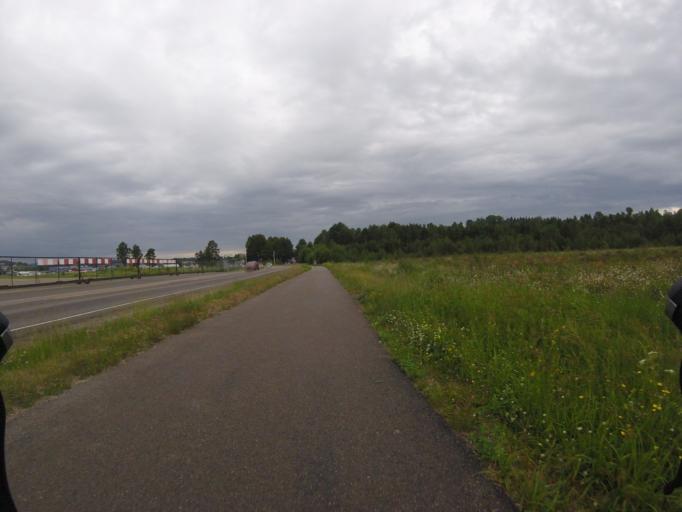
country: NO
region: Akershus
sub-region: Skedsmo
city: Lillestrom
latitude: 59.9651
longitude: 11.0521
